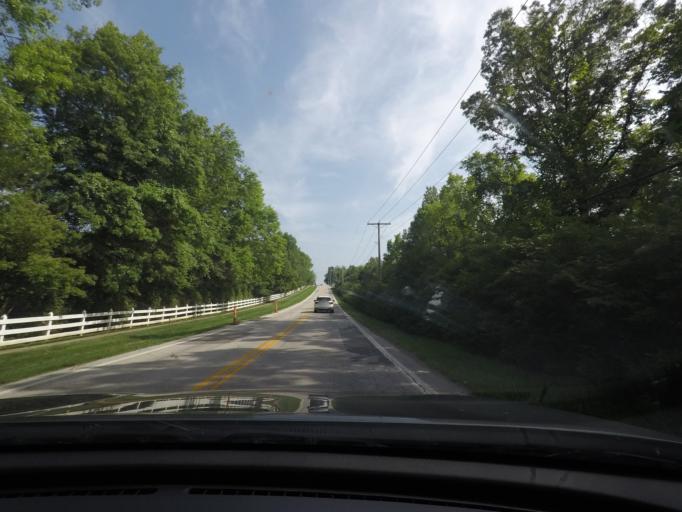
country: US
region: Missouri
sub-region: Saint Louis County
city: Town and Country
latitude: 38.6336
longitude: -90.4810
